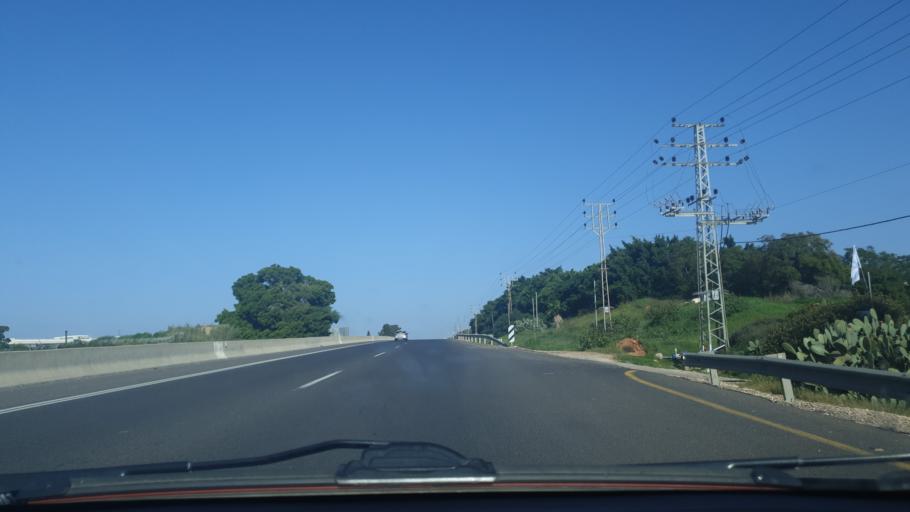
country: IL
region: Central District
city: Bet Dagan
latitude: 31.9930
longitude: 34.8271
